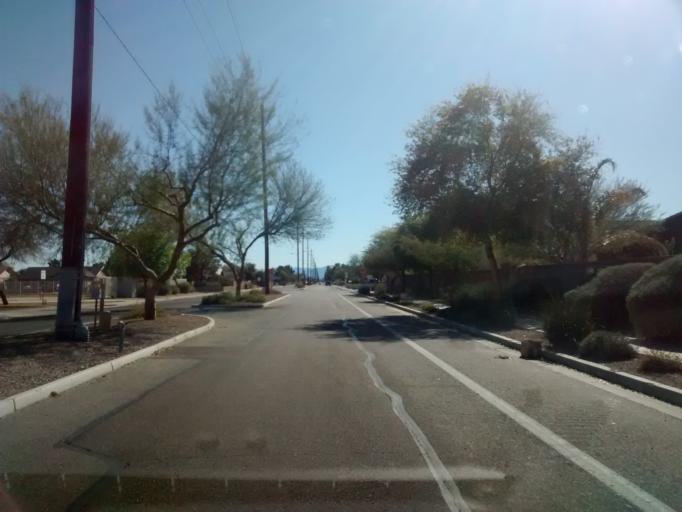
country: US
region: Arizona
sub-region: Maricopa County
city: Glendale
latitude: 33.5355
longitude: -112.2119
